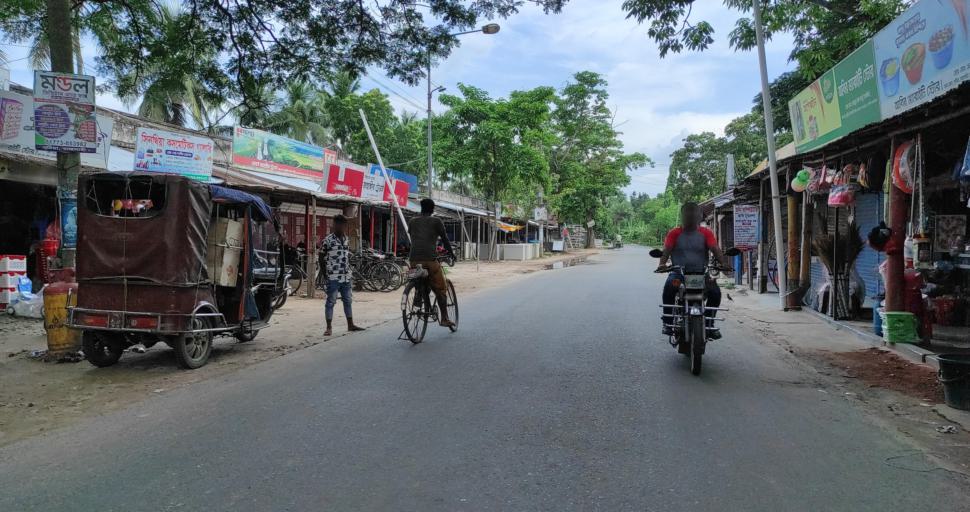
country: BD
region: Rajshahi
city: Rajshahi
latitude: 24.3710
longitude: 88.8389
